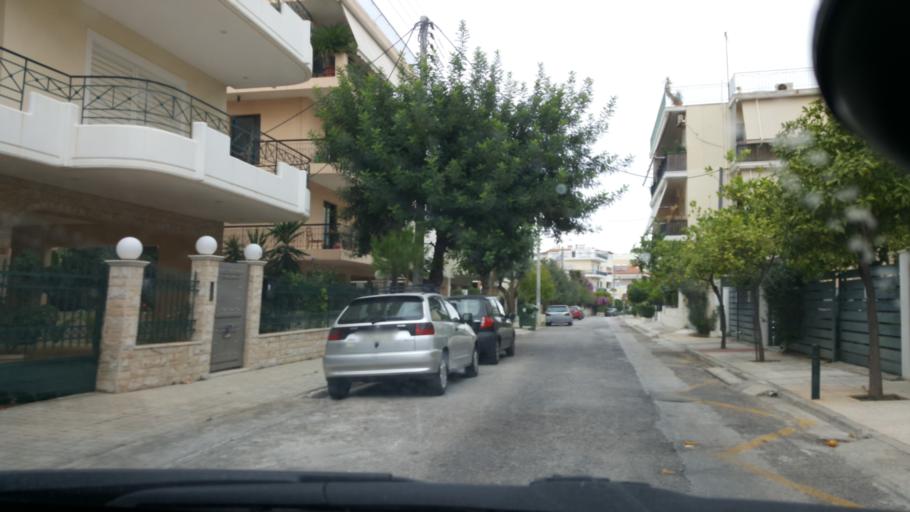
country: GR
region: Attica
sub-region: Nomarchia Athinas
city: Argyroupoli
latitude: 37.8942
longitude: 23.7498
